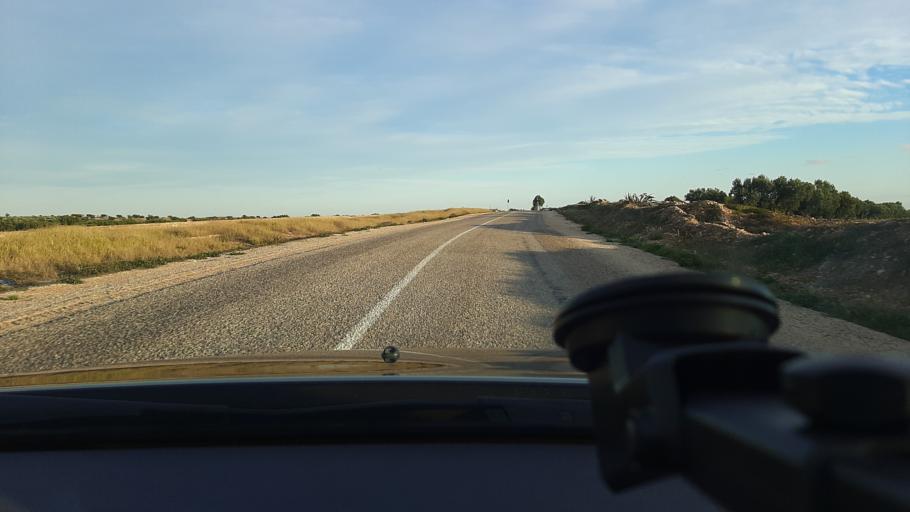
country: TN
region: Safaqis
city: Sfax
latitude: 34.9550
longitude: 10.5477
